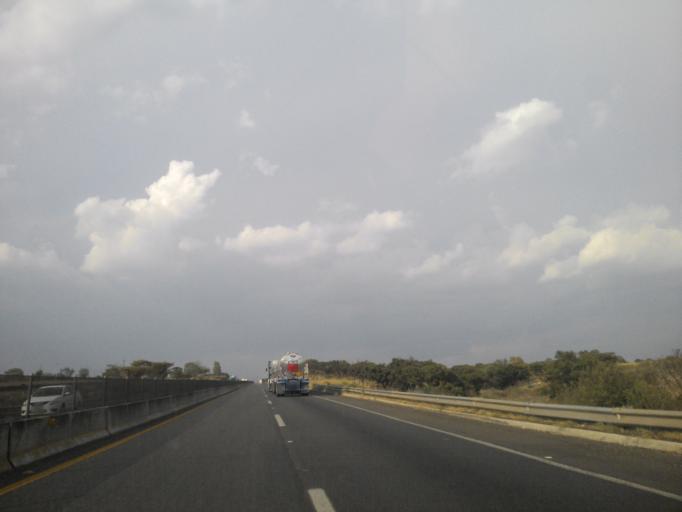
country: MX
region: Jalisco
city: Tepatitlan de Morelos
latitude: 20.8487
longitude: -102.7783
